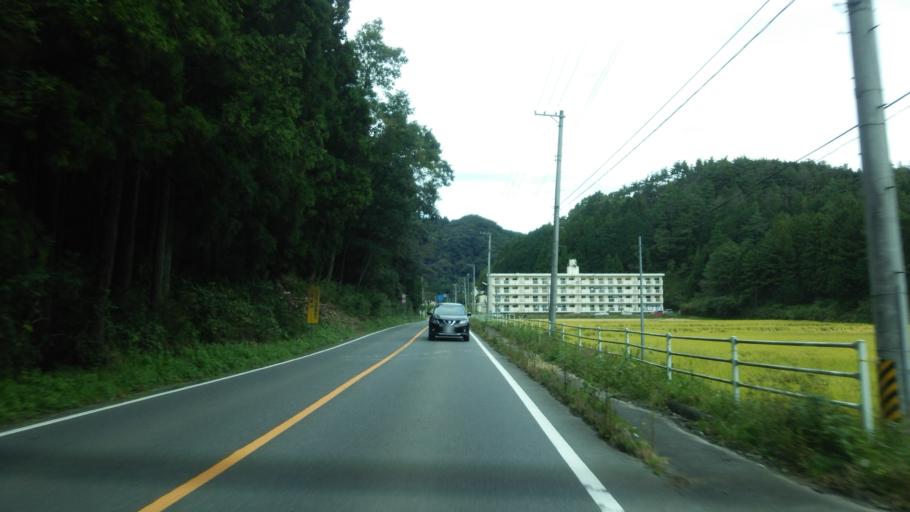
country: JP
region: Fukushima
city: Sukagawa
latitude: 37.1782
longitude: 140.2164
